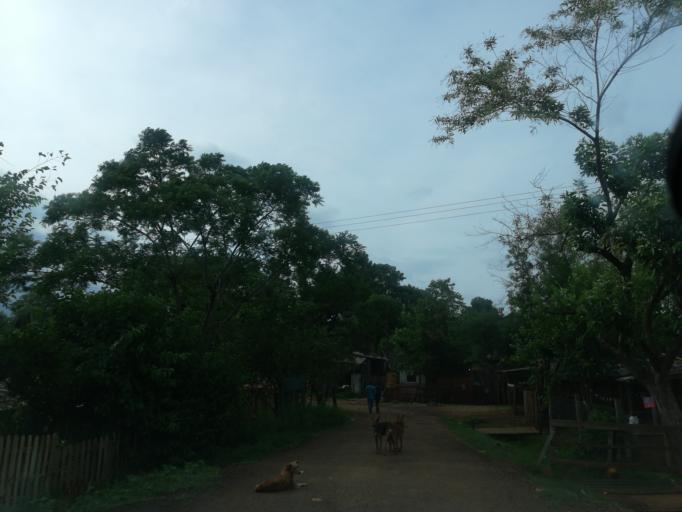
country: AR
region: Misiones
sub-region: Departamento de Capital
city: Posadas
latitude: -27.4202
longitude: -55.9154
